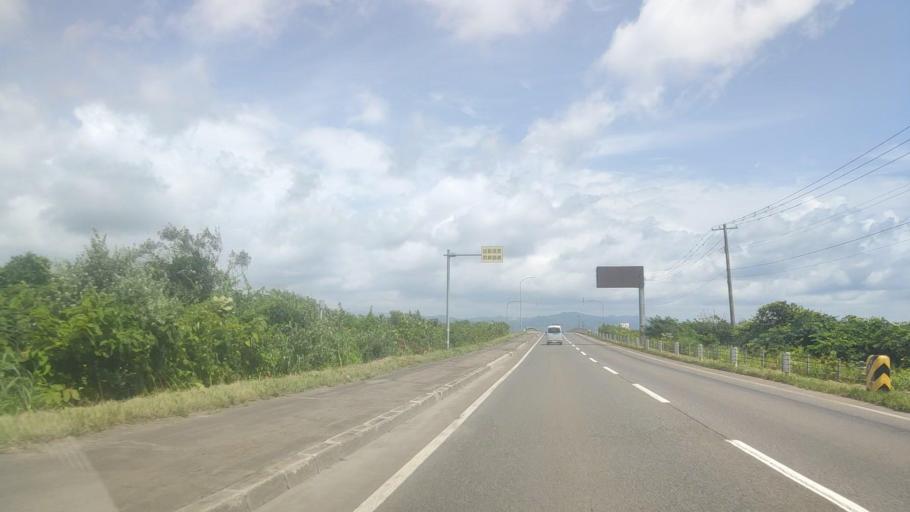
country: JP
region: Hokkaido
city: Niseko Town
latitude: 42.5226
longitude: 140.3859
